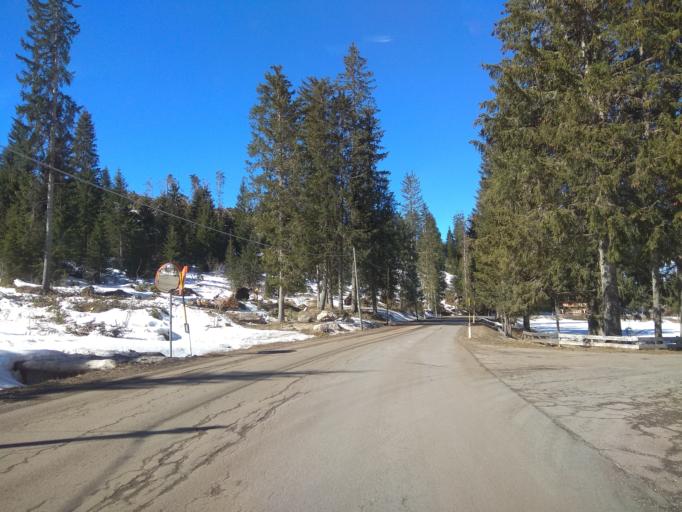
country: IT
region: Trentino-Alto Adige
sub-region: Bolzano
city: Nova Levante
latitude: 46.4062
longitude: 11.5848
